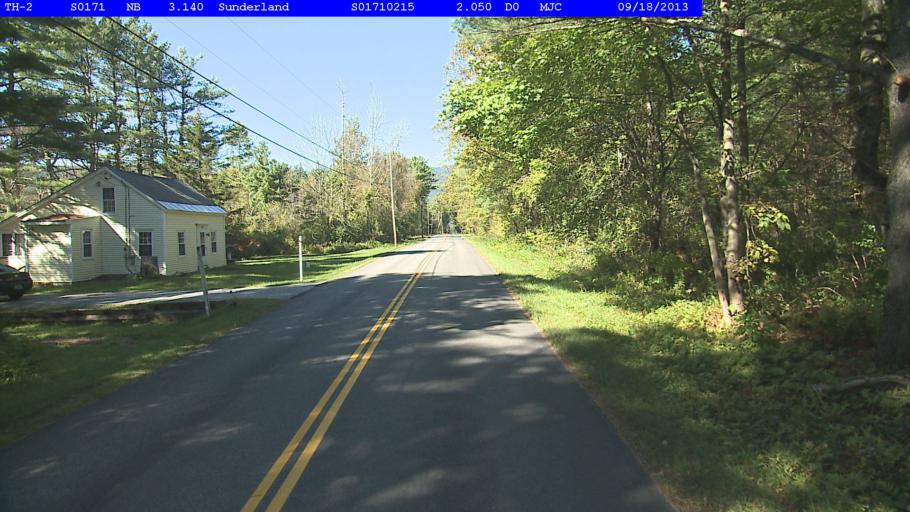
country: US
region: Vermont
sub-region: Bennington County
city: Arlington
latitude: 43.0942
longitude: -73.1237
